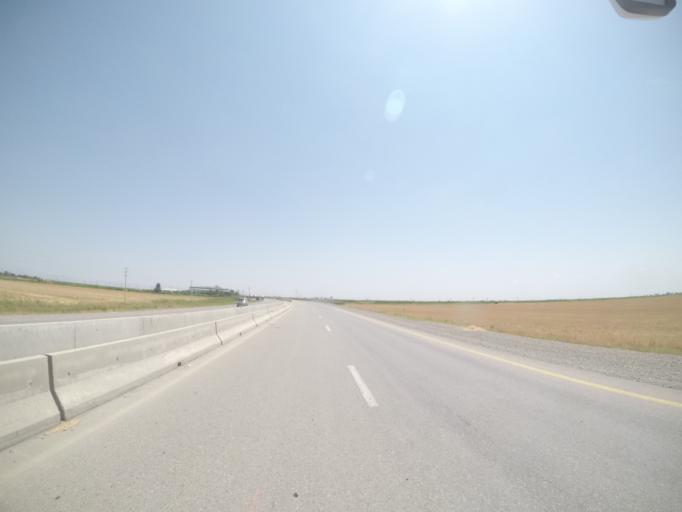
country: AZ
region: Kurdamir Rayon
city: Kyurdarmir
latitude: 40.3141
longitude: 48.1661
